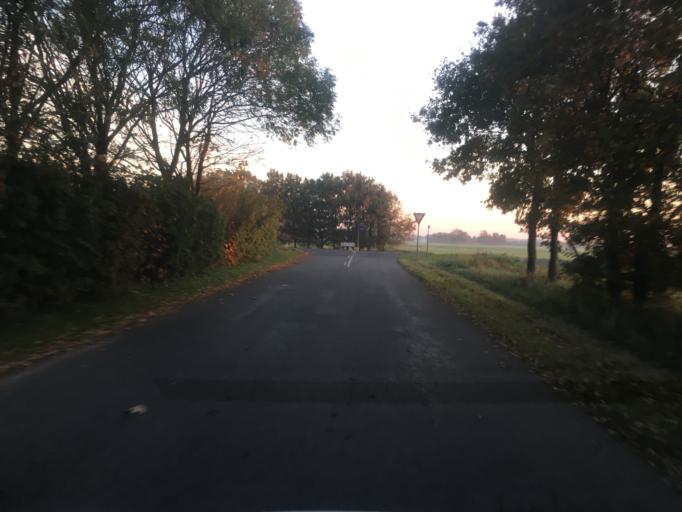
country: DK
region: South Denmark
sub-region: Tonder Kommune
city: Logumkloster
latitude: 55.0305
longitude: 9.0496
